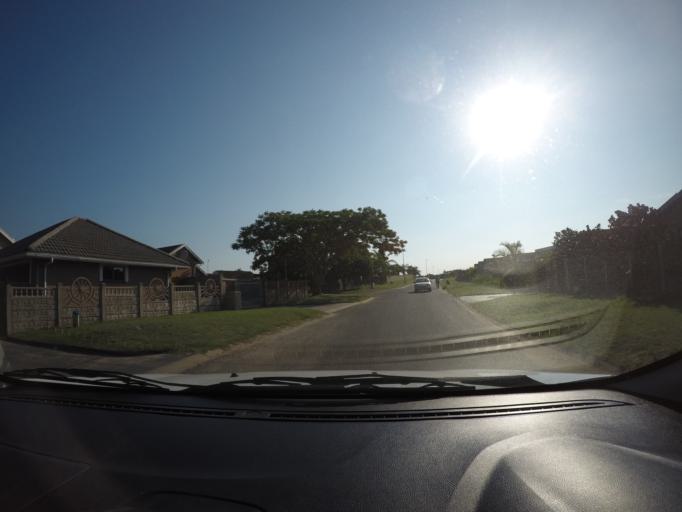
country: ZA
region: KwaZulu-Natal
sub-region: uThungulu District Municipality
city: Richards Bay
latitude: -28.7147
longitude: 32.0370
